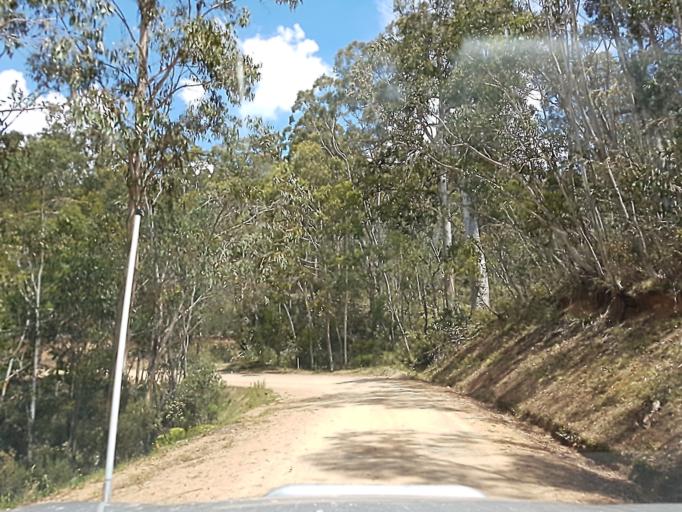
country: AU
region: New South Wales
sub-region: Snowy River
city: Jindabyne
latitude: -36.8865
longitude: 148.0842
